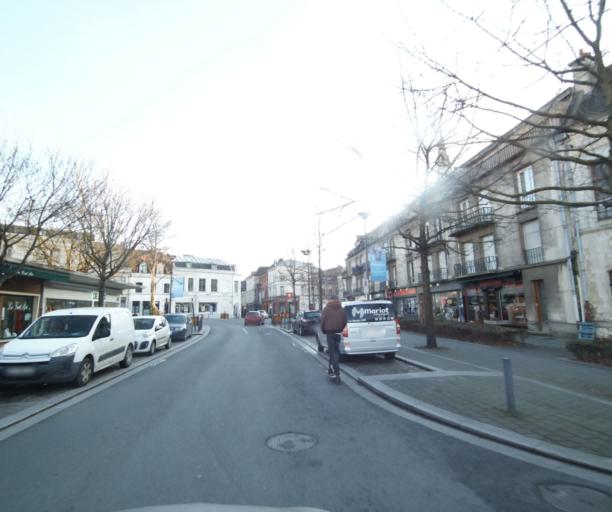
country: FR
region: Nord-Pas-de-Calais
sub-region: Departement du Nord
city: Valenciennes
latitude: 50.3568
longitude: 3.5269
